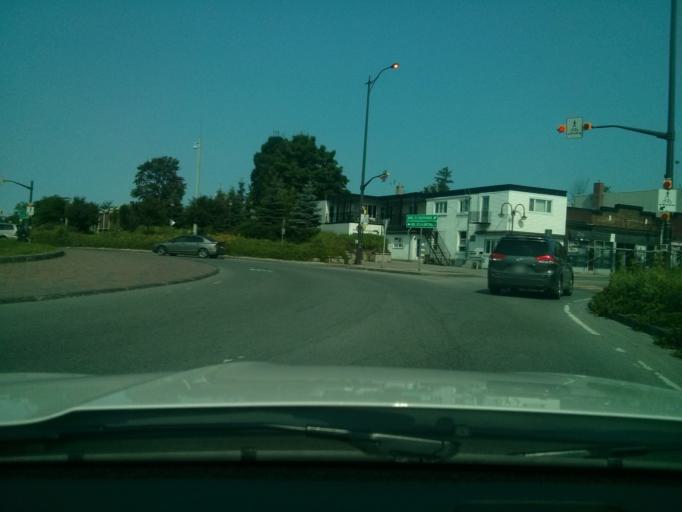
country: CA
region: Ontario
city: Ottawa
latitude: 45.4323
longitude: -75.7328
